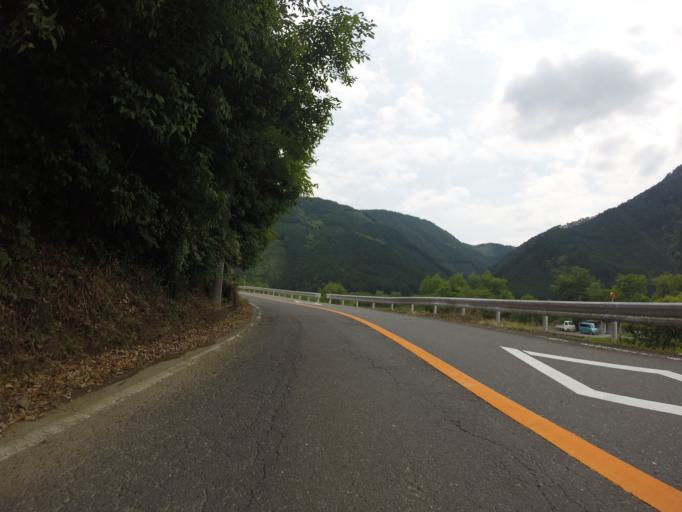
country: JP
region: Shizuoka
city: Shizuoka-shi
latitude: 35.1102
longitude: 138.3426
